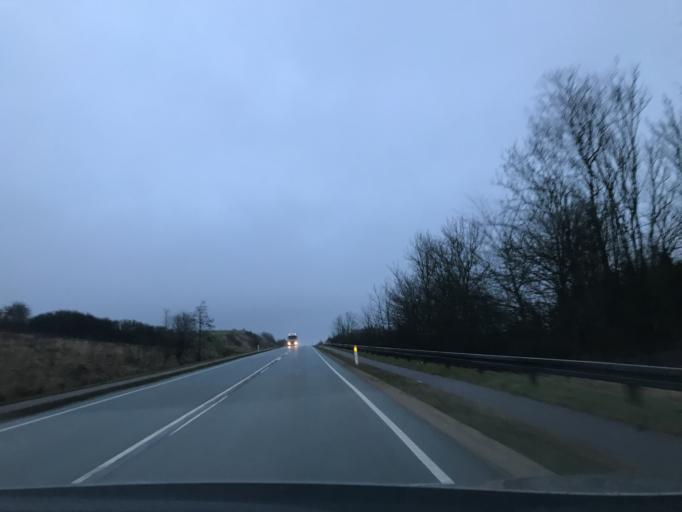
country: DK
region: Central Jutland
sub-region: Hedensted Kommune
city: Hedensted
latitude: 55.7067
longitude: 9.7513
